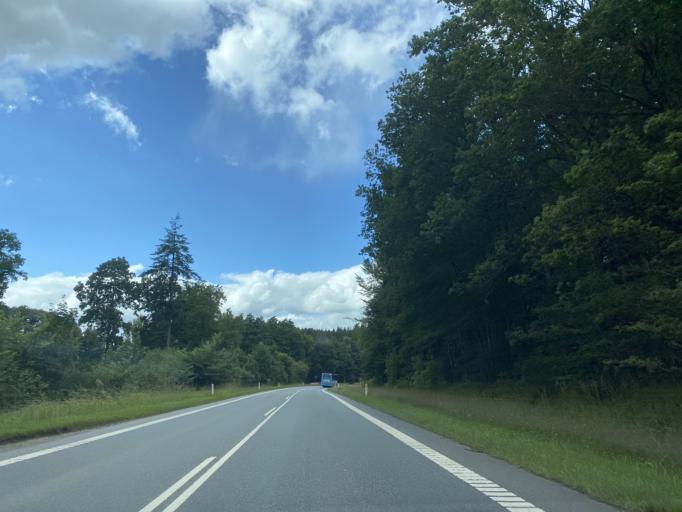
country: DK
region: Central Jutland
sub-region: Silkeborg Kommune
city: Silkeborg
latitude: 56.2632
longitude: 9.6212
